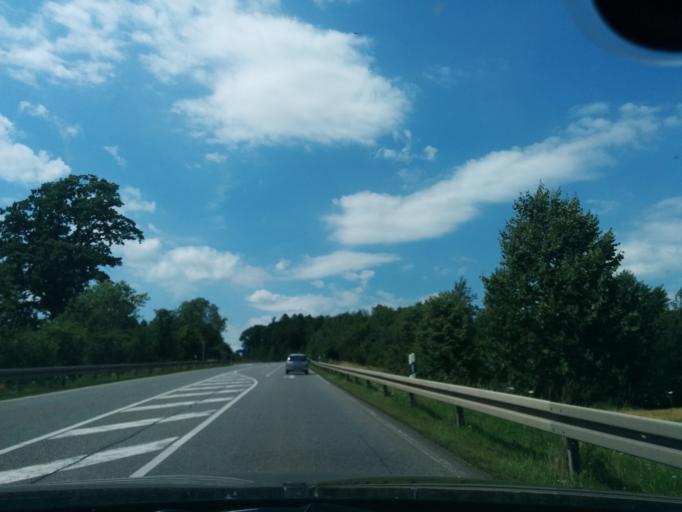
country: DE
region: Saxony
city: Hainichen
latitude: 50.9845
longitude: 13.1017
